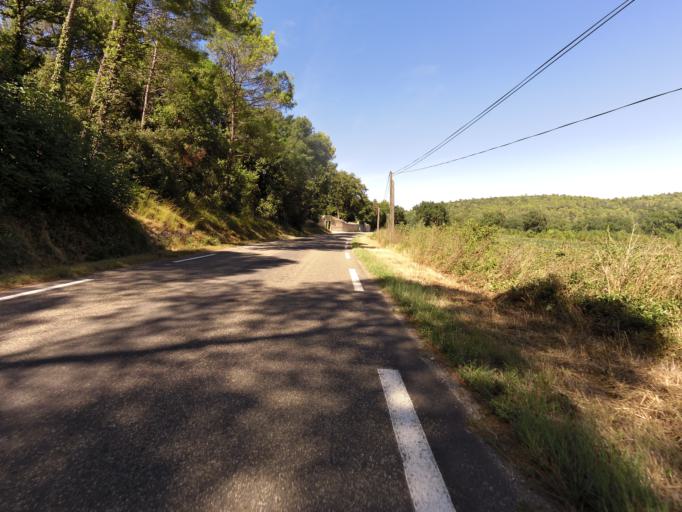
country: FR
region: Languedoc-Roussillon
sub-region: Departement du Gard
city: Sommieres
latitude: 43.8144
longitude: 4.0676
